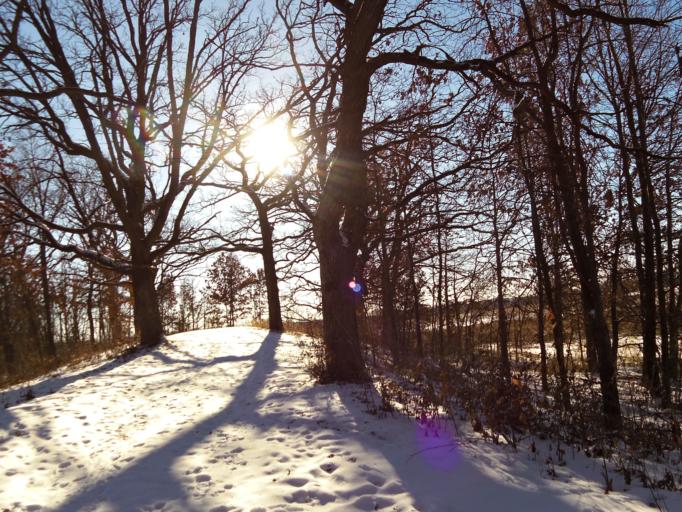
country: US
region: Minnesota
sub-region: Washington County
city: Lake Elmo
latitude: 44.9847
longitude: -92.9108
